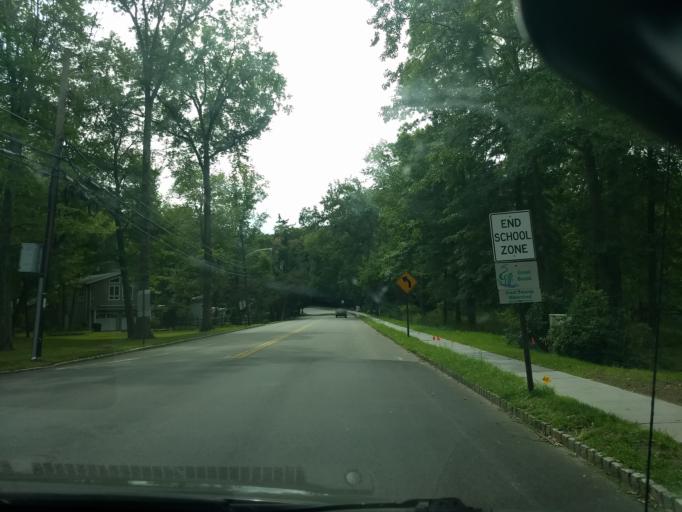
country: US
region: New Jersey
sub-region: Morris County
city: Morristown
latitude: 40.7848
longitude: -74.4796
